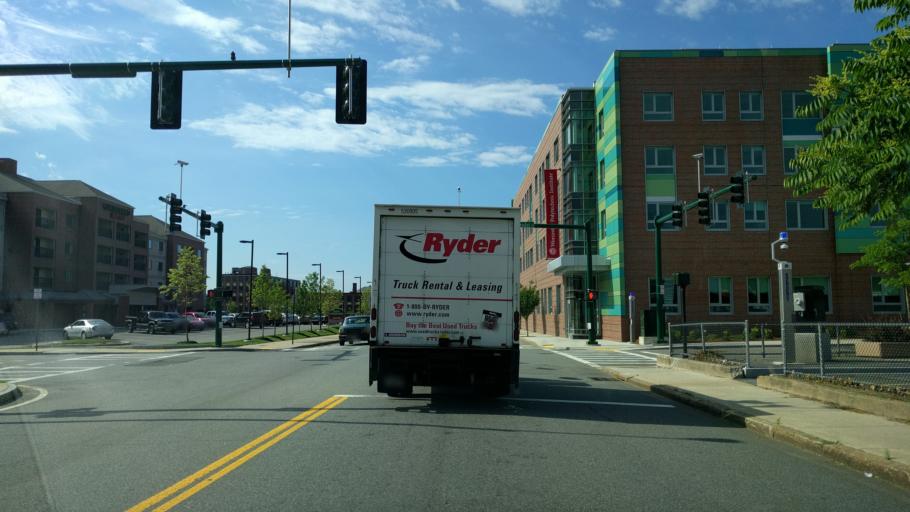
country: US
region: Massachusetts
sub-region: Worcester County
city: Worcester
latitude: 42.2757
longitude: -71.8008
